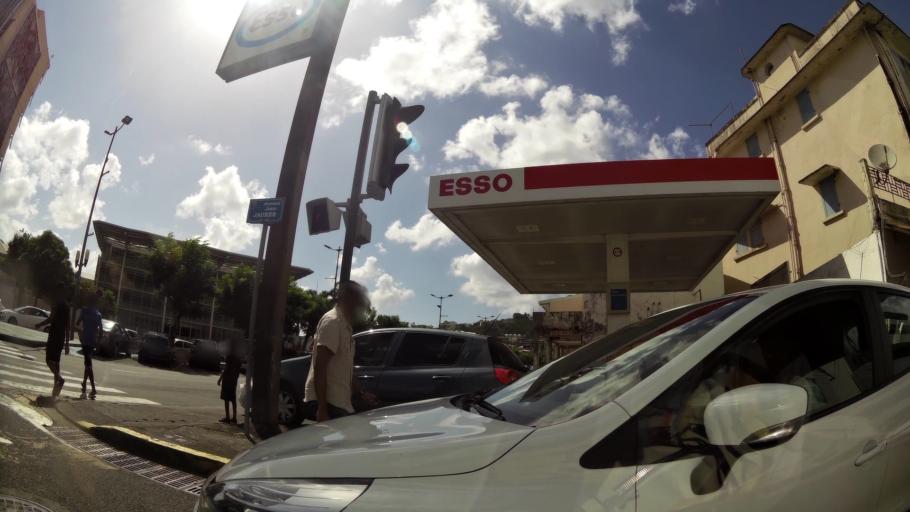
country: MQ
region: Martinique
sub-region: Martinique
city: Fort-de-France
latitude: 14.6079
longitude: -61.0698
